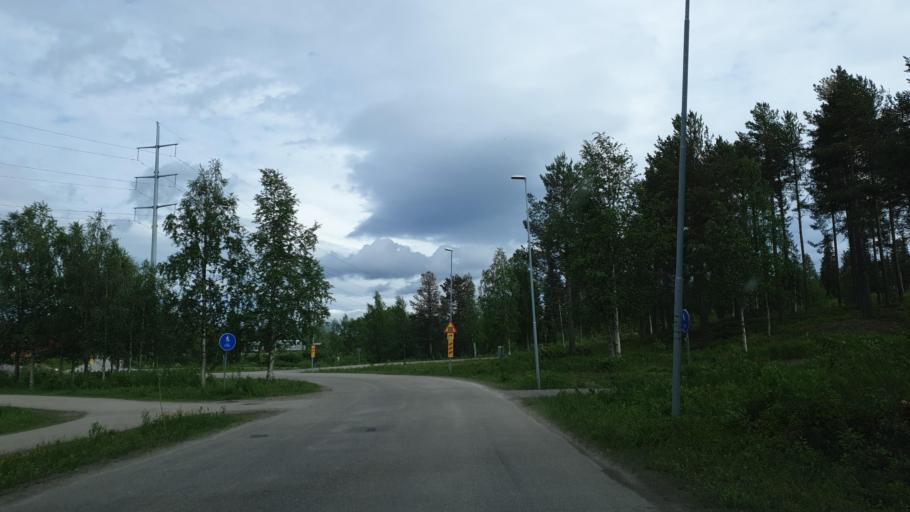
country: SE
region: Norrbotten
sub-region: Gallivare Kommun
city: Gaellivare
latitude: 67.1273
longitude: 20.6563
